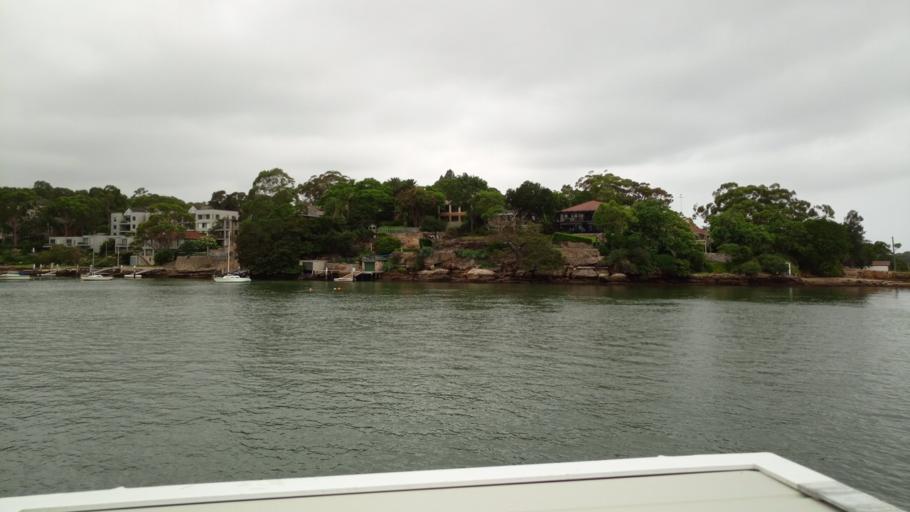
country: AU
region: New South Wales
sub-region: Hunters Hill
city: Gladesville
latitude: -33.8443
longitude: 151.1319
